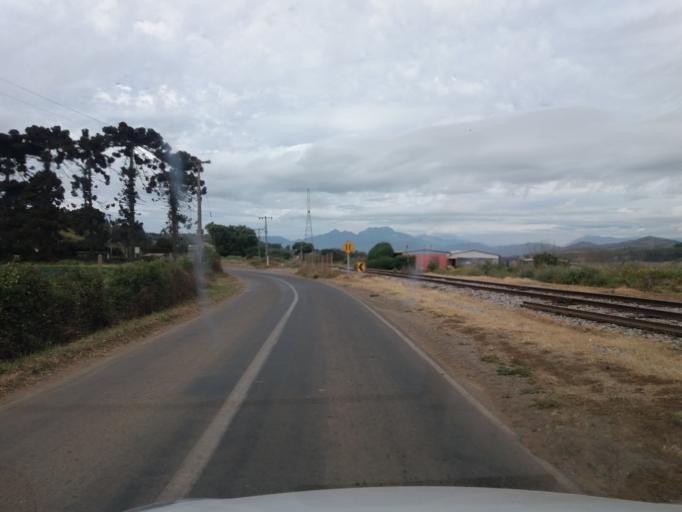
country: CL
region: Valparaiso
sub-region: Provincia de Marga Marga
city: Villa Alemana
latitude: -32.9168
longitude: -71.4042
